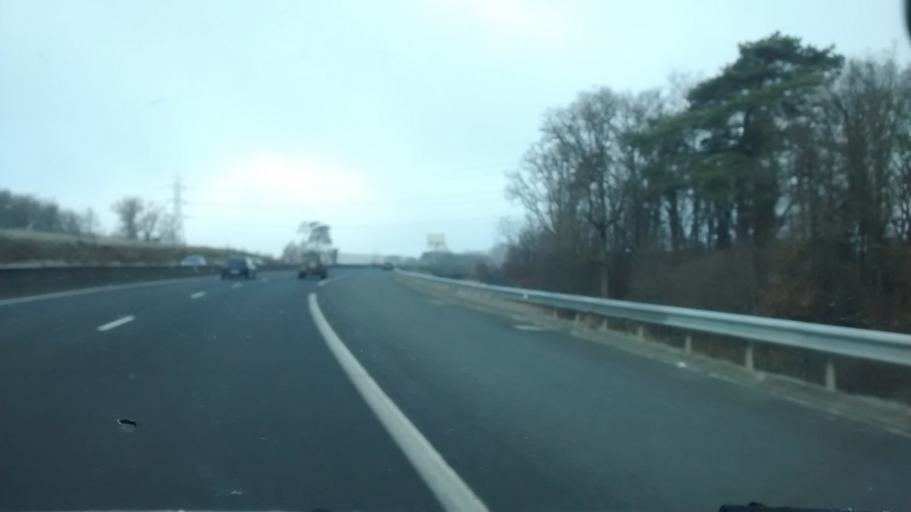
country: FR
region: Centre
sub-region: Departement d'Indre-et-Loire
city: Chambray-les-Tours
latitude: 47.3223
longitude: 0.6989
